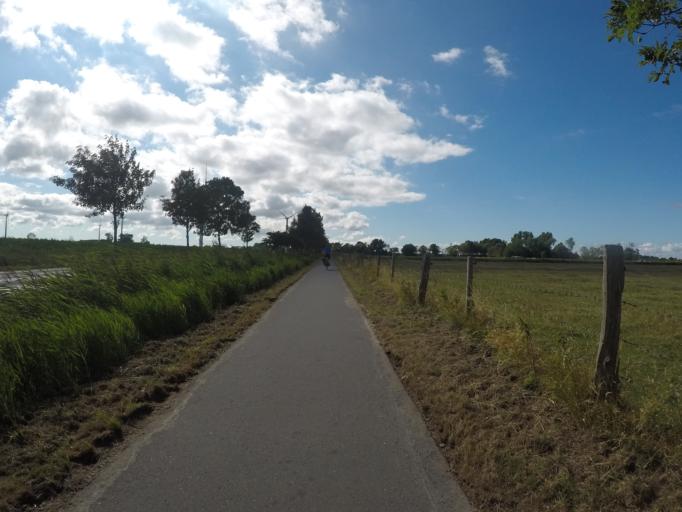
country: DE
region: Lower Saxony
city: Osterbruch
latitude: 53.7869
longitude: 8.9306
